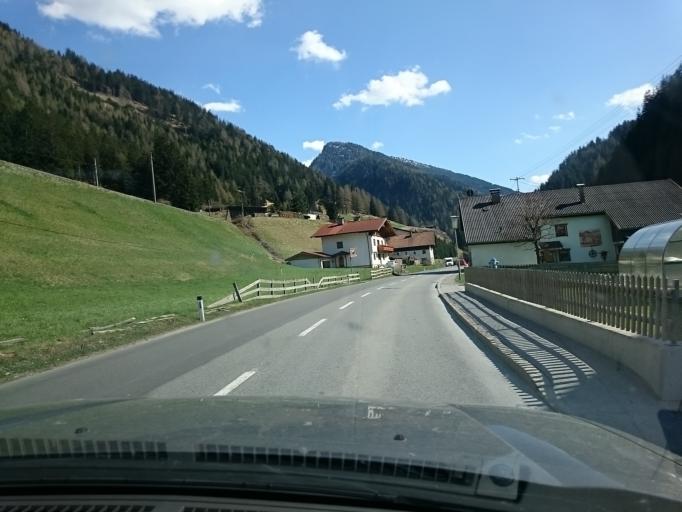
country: AT
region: Tyrol
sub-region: Politischer Bezirk Innsbruck Land
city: Steinach am Brenner
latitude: 47.0732
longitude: 11.4842
